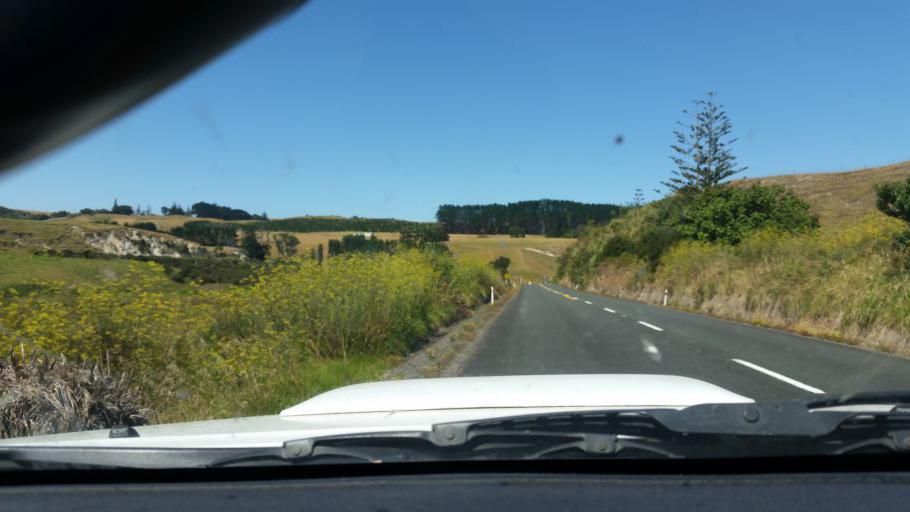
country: NZ
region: Northland
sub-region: Kaipara District
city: Dargaville
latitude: -35.8325
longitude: 173.6630
